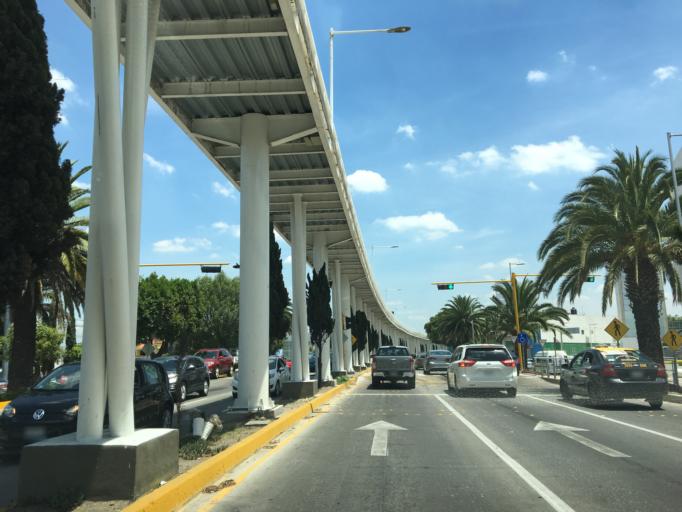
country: MX
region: Puebla
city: Puebla
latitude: 19.0706
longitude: -98.2261
